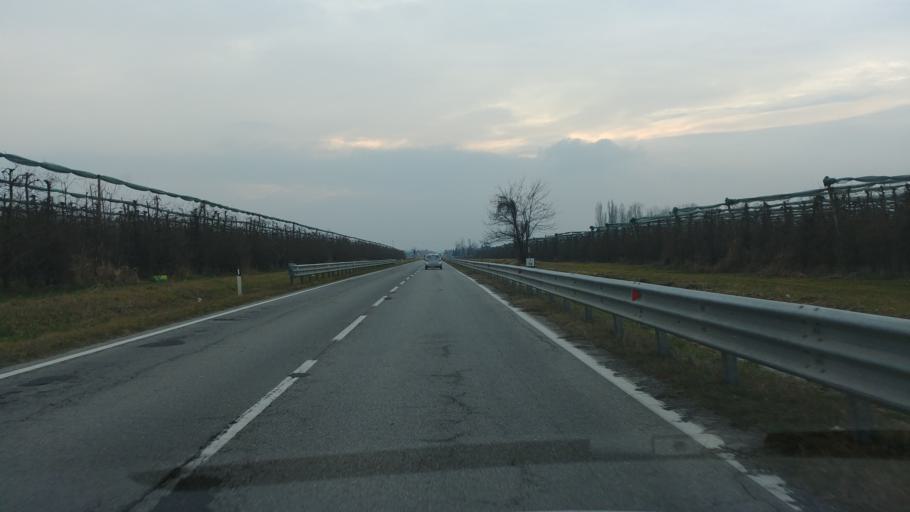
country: IT
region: Piedmont
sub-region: Provincia di Cuneo
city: Castelletto Stura
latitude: 44.4410
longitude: 7.6024
